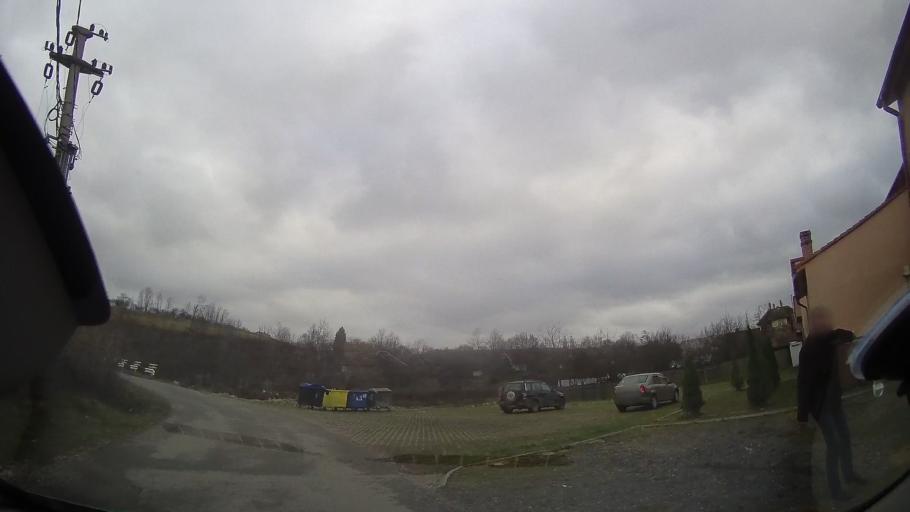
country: RO
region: Cluj
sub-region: Comuna Calatele
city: Calatele
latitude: 46.7686
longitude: 23.0096
